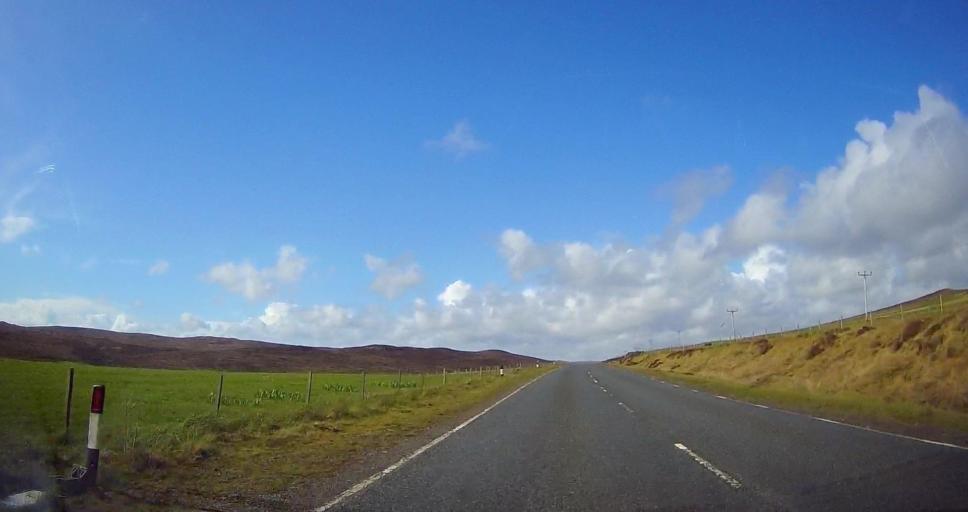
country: GB
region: Scotland
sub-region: Shetland Islands
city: Lerwick
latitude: 60.2003
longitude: -1.2328
